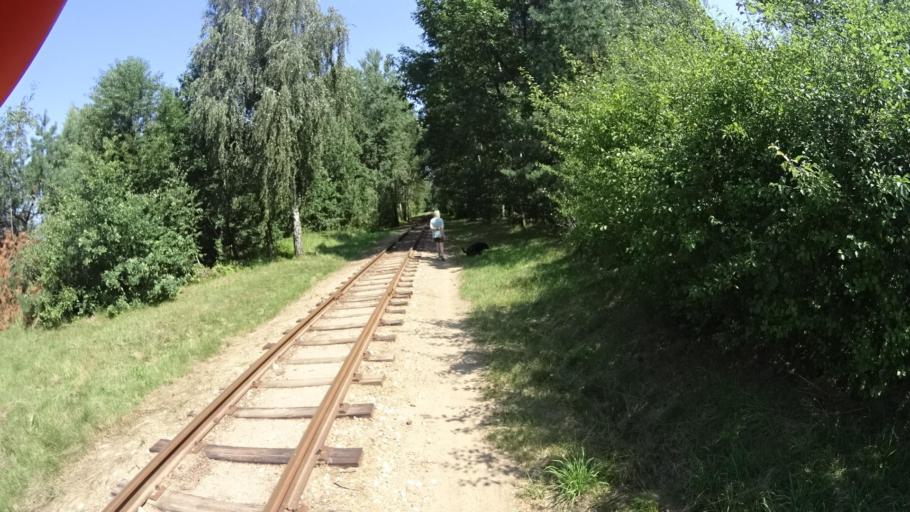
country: PL
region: Masovian Voivodeship
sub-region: Powiat piaseczynski
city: Tarczyn
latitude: 51.9869
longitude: 20.8831
